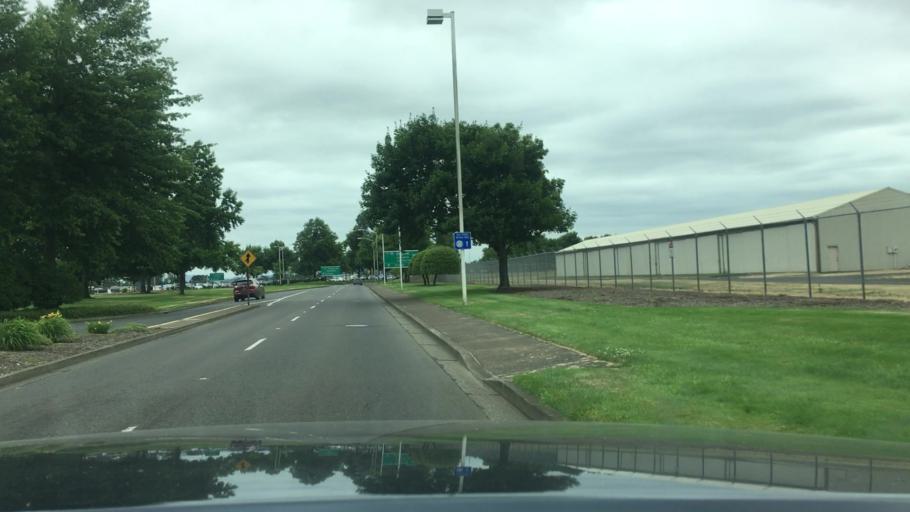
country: US
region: Oregon
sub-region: Lane County
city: Junction City
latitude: 44.1171
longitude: -123.2108
